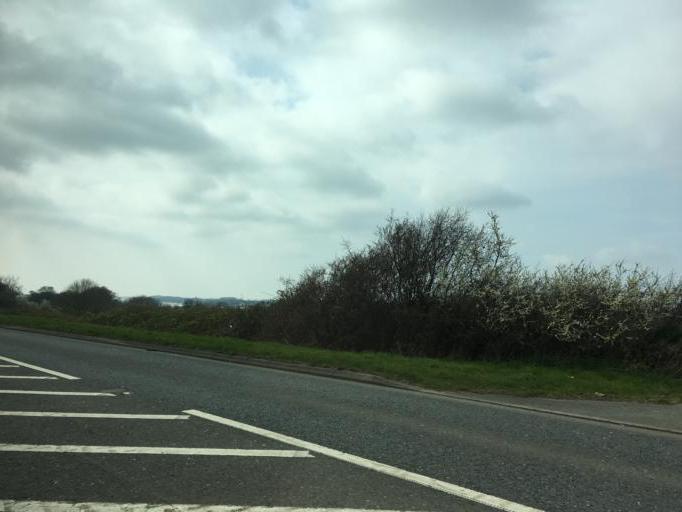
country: GB
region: Wales
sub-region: Gwynedd
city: Caernarfon
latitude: 53.1613
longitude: -4.2492
